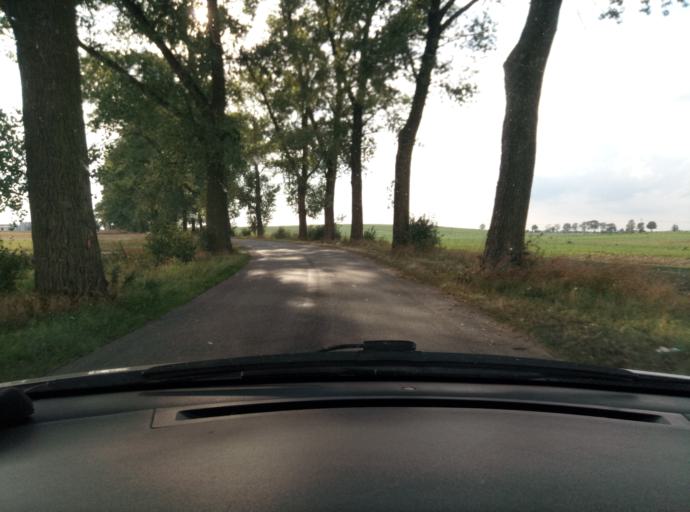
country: PL
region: Kujawsko-Pomorskie
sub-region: Powiat brodnicki
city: Jablonowo Pomorskie
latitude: 53.3869
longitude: 19.1880
